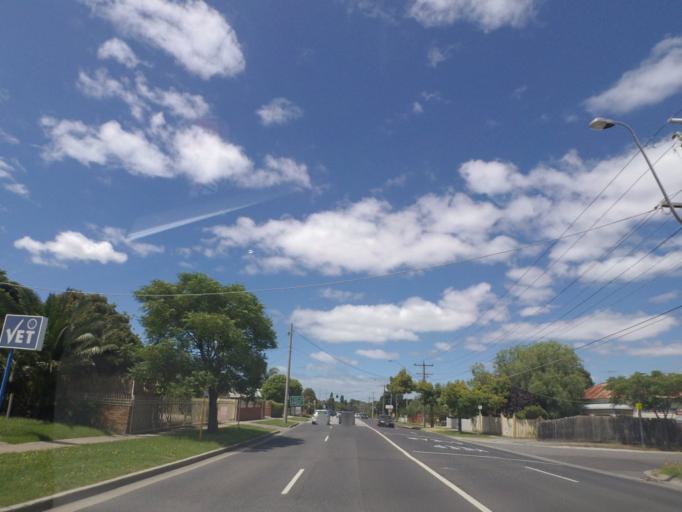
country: AU
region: Victoria
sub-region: Brimbank
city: Sunshine West
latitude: -37.7866
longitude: 144.8272
